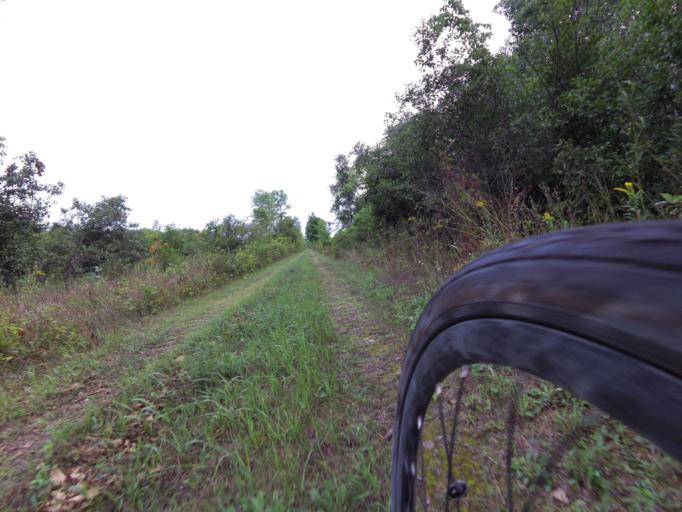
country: CA
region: Ontario
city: Perth
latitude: 44.6280
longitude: -76.2423
